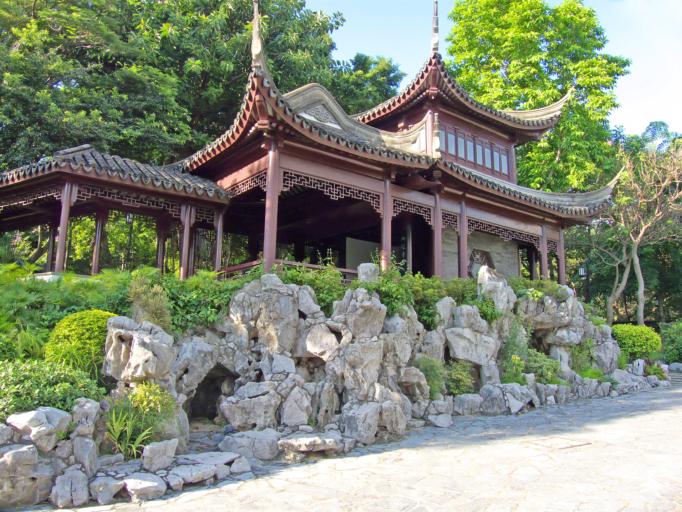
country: HK
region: Kowloon City
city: Kowloon
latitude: 22.3317
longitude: 114.1894
